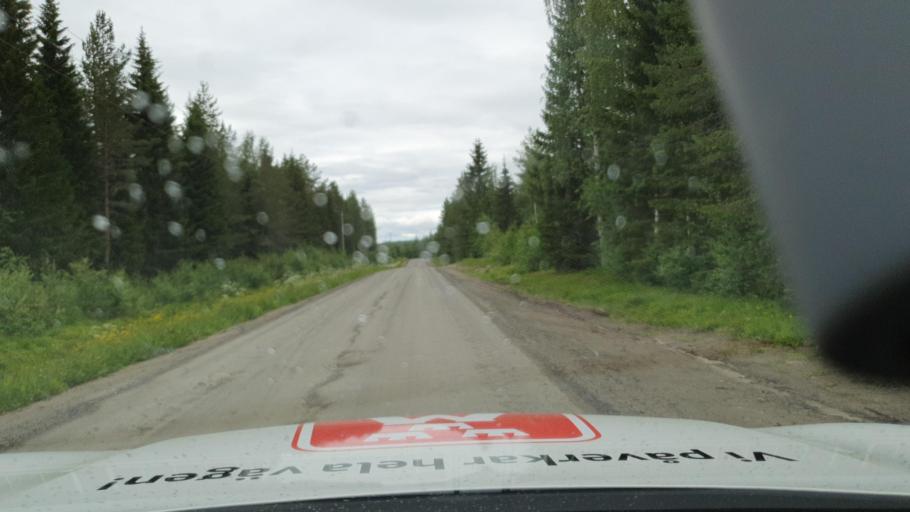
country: SE
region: Vaesterbotten
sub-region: Nordmalings Kommun
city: Nordmaling
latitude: 63.6547
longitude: 19.4400
